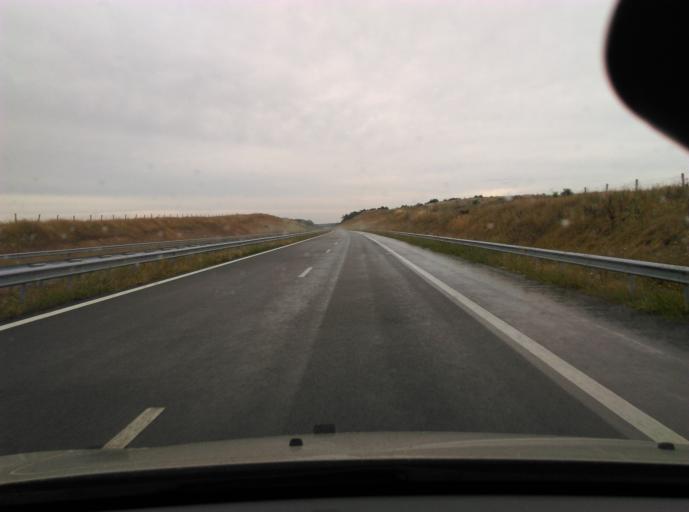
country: BG
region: Khaskovo
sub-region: Obshtina Dimitrovgrad
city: Dimitrovgrad
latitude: 42.0403
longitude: 25.5279
